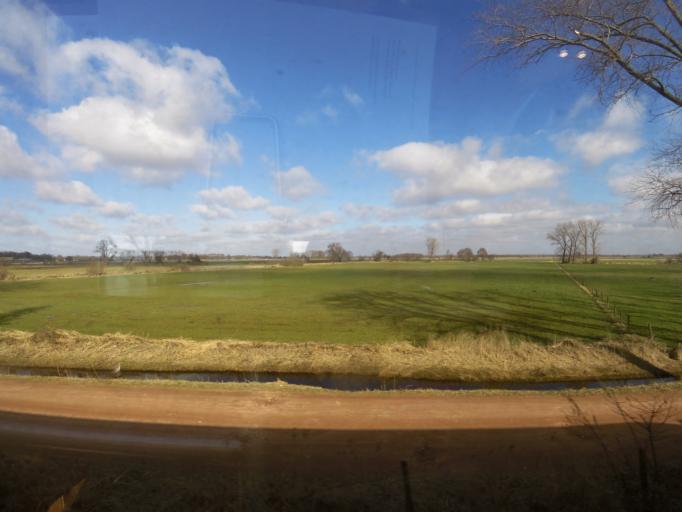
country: DE
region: Lower Saxony
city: Oyten
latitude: 53.0846
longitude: 8.9626
